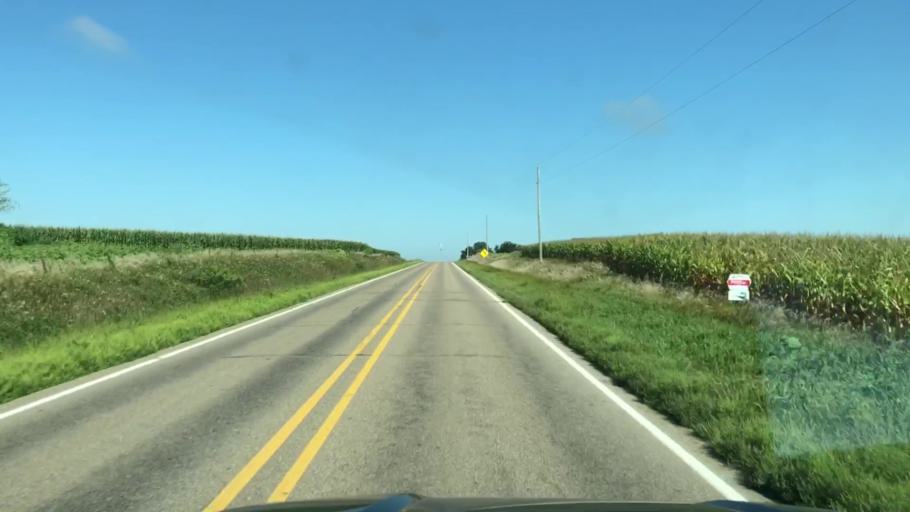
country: US
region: Iowa
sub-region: Woodbury County
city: Sergeant Bluff
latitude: 42.4282
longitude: -96.2814
